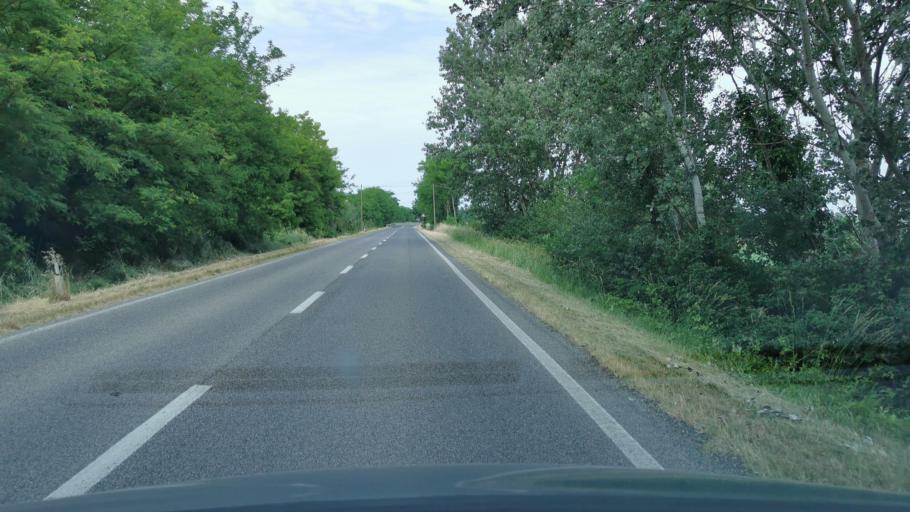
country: IT
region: Emilia-Romagna
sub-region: Provincia di Ravenna
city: Savarna-Conventella
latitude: 44.5242
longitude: 12.1118
